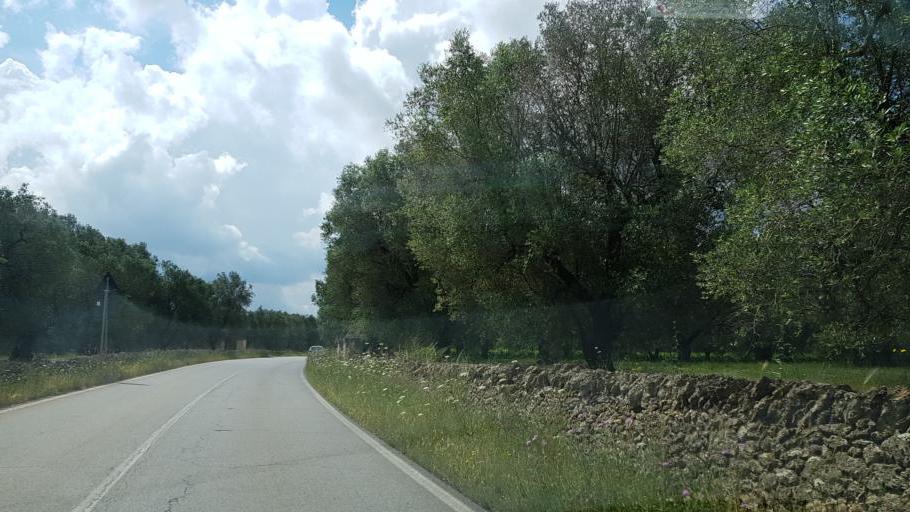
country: IT
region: Apulia
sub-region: Provincia di Brindisi
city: Mesagne
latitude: 40.5172
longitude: 17.8253
